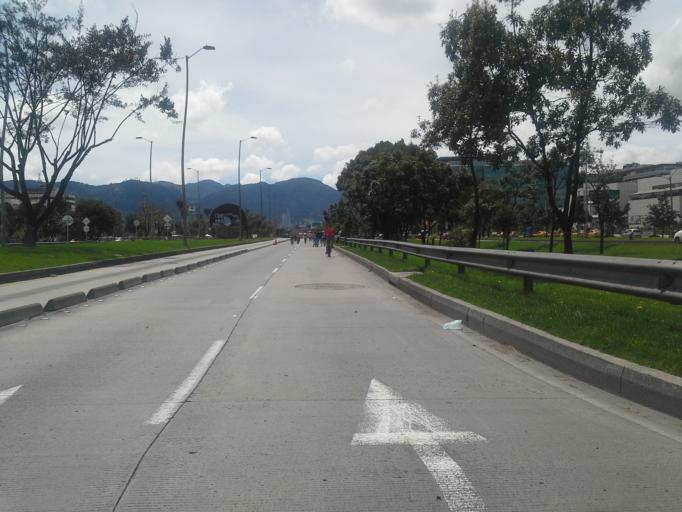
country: CO
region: Bogota D.C.
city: Bogota
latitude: 4.6494
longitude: -74.1008
